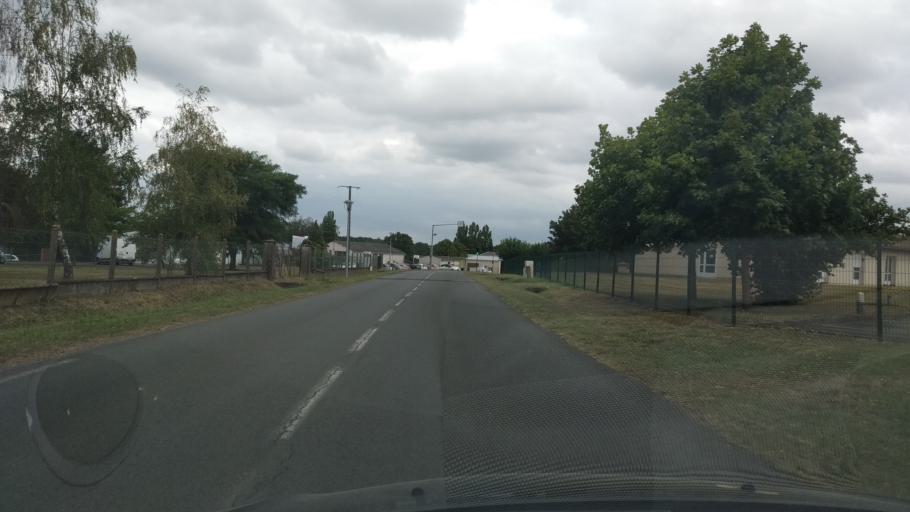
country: FR
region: Poitou-Charentes
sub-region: Departement de la Vienne
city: Smarves
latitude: 46.5073
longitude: 0.3588
